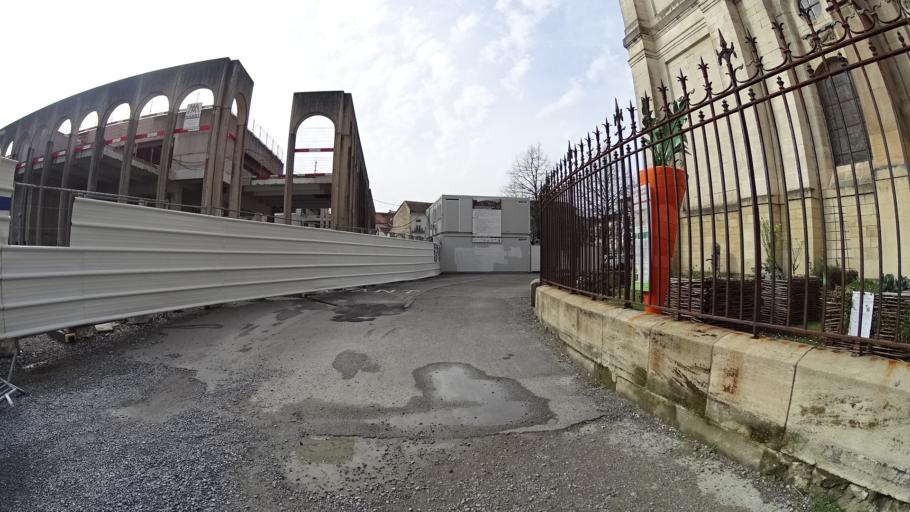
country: FR
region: Aquitaine
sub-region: Departement des Landes
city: Dax
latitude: 43.7082
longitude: -1.0532
